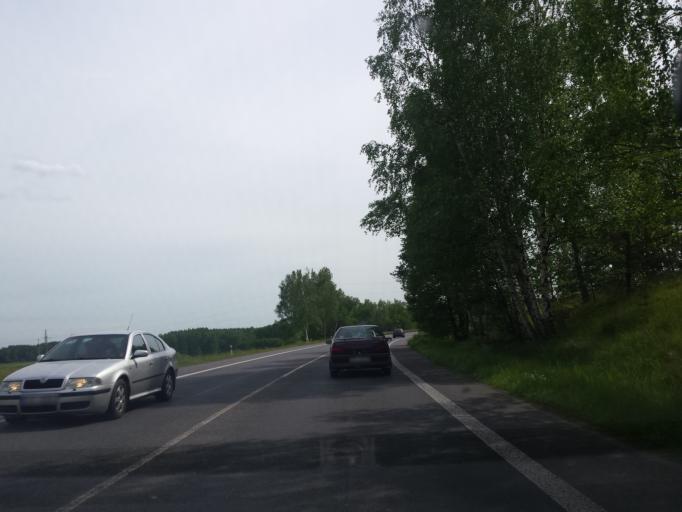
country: CZ
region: Liberecky
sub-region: Okres Ceska Lipa
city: Ceska Lipa
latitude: 50.6687
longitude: 14.5433
